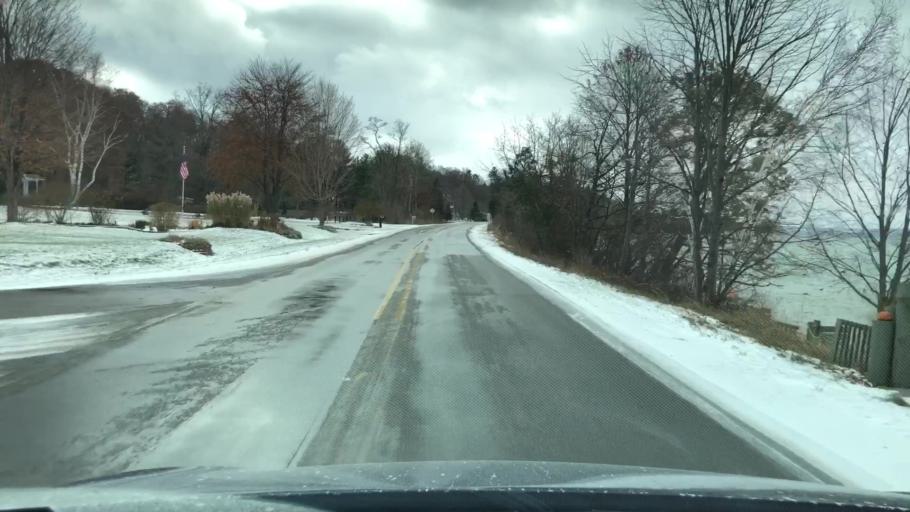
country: US
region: Michigan
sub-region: Leelanau County
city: Greilickville
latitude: 44.8455
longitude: -85.5574
